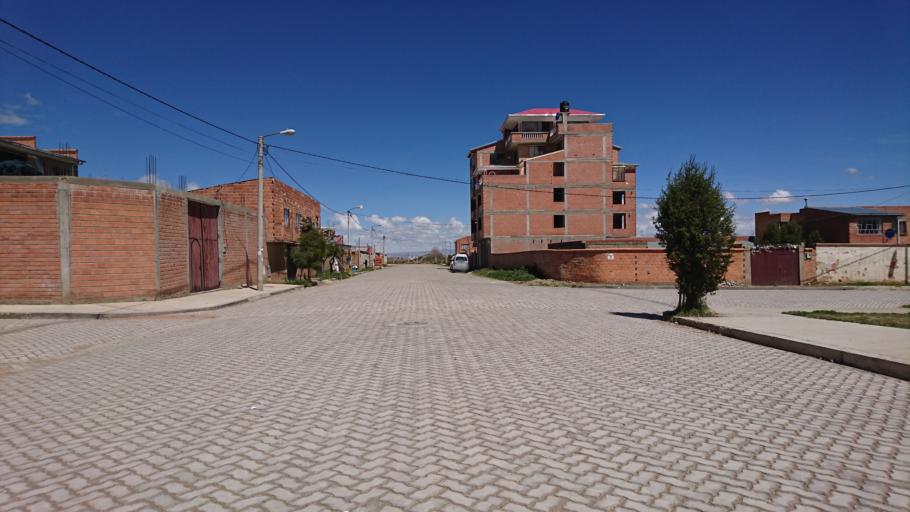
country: BO
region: La Paz
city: La Paz
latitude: -16.5023
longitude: -68.1881
